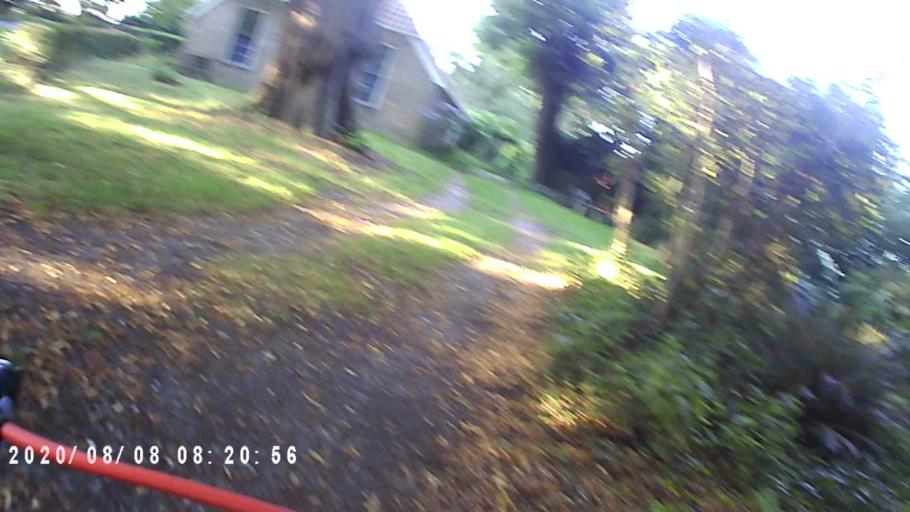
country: NL
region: Groningen
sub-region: Gemeente Leek
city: Leek
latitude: 53.0931
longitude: 6.3137
